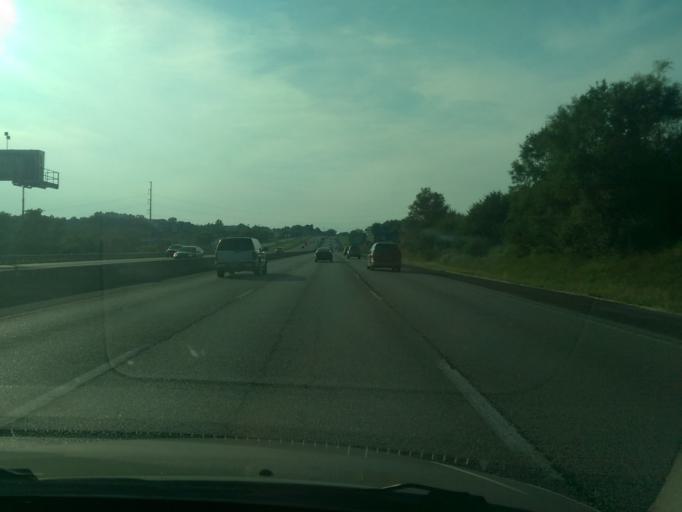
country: US
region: Missouri
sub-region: Platte County
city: Riverside
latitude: 39.1999
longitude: -94.6258
